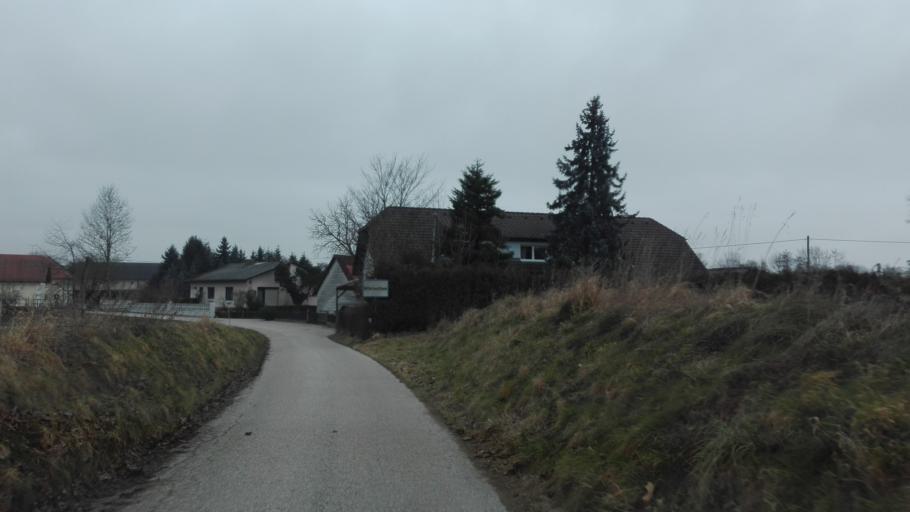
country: AT
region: Upper Austria
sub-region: Wels-Land
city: Holzhausen
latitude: 48.2208
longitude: 14.1350
